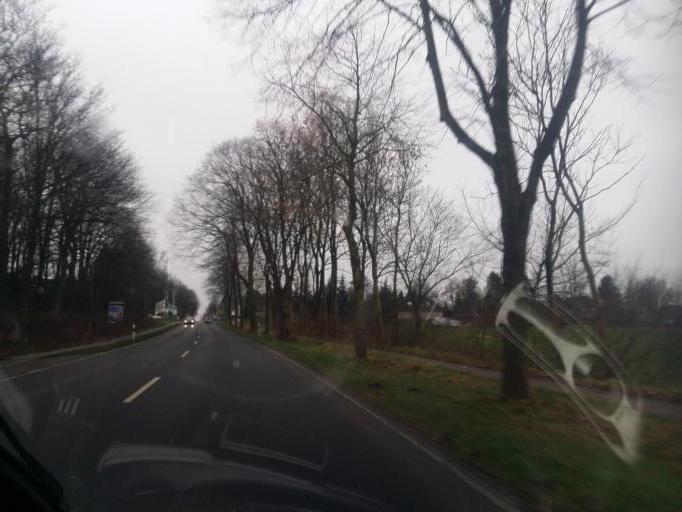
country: DE
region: Schleswig-Holstein
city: Heide
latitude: 54.2133
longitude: 9.1135
